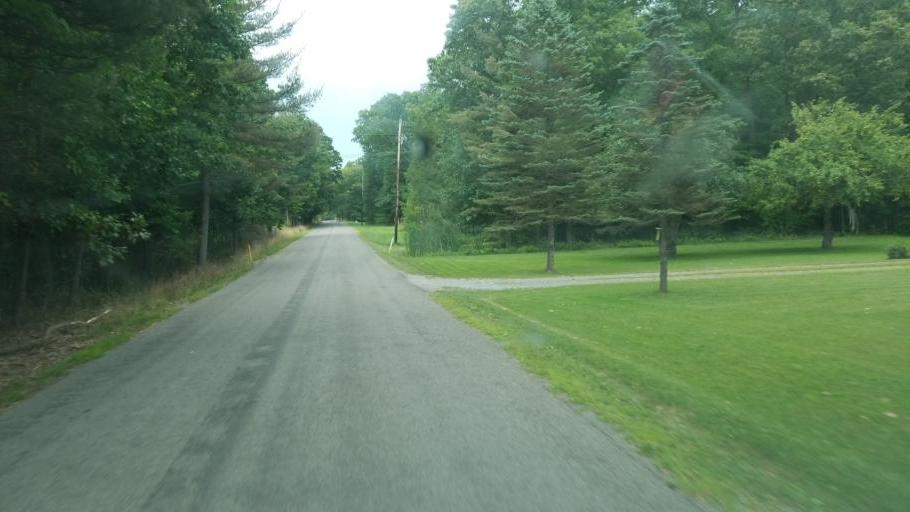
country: US
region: Pennsylvania
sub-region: Clarion County
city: Marianne
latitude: 41.2036
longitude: -79.4419
